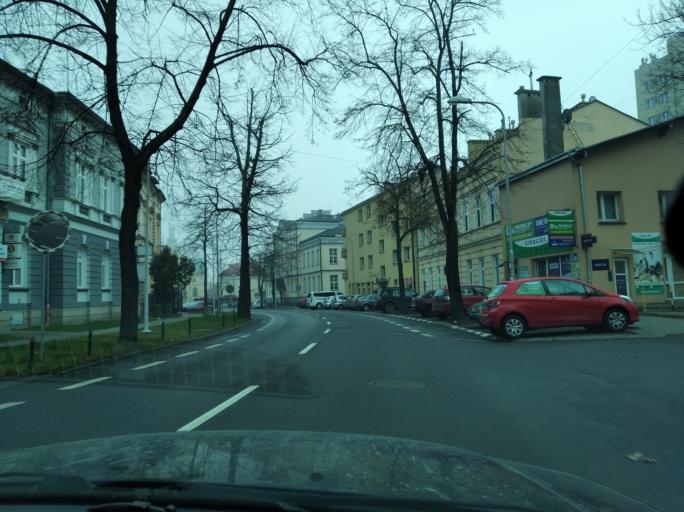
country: PL
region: Subcarpathian Voivodeship
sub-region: Rzeszow
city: Rzeszow
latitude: 50.0399
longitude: 21.9965
